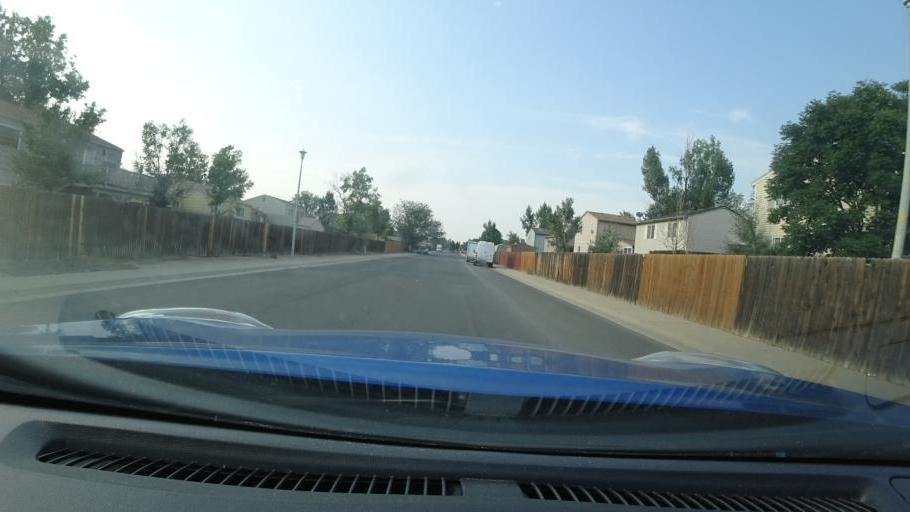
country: US
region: Colorado
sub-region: Adams County
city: Aurora
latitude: 39.7444
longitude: -104.7630
